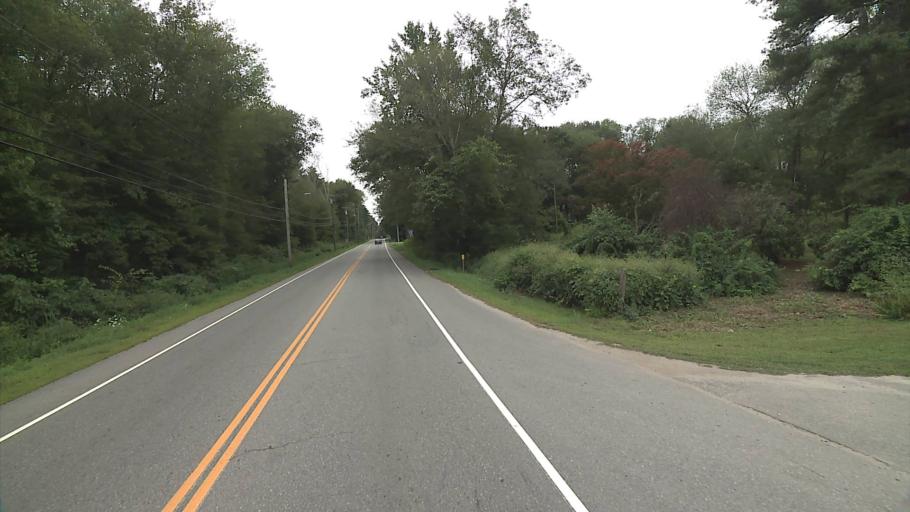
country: US
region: Connecticut
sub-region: New London County
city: Montville Center
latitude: 41.4238
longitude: -72.2053
